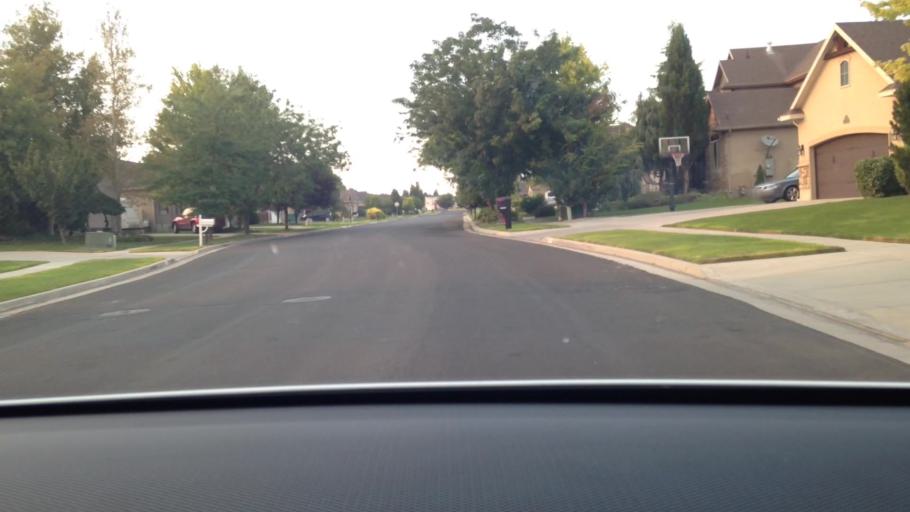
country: US
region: Utah
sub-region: Davis County
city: Clearfield
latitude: 41.0751
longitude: -112.0102
